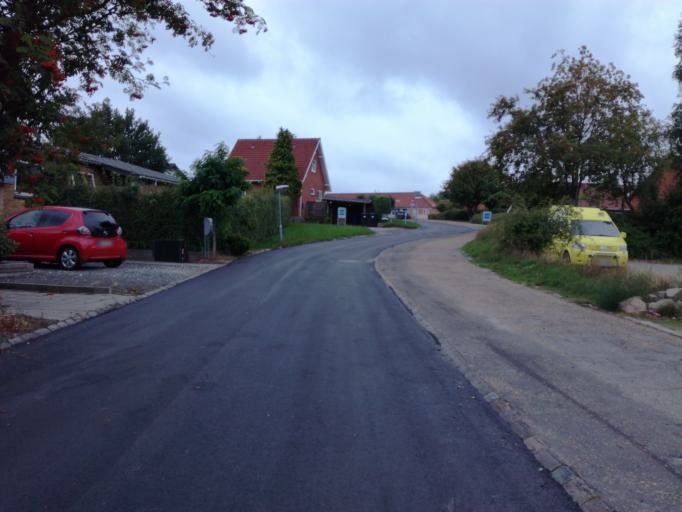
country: DK
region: South Denmark
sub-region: Vejle Kommune
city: Borkop
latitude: 55.6432
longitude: 9.6469
